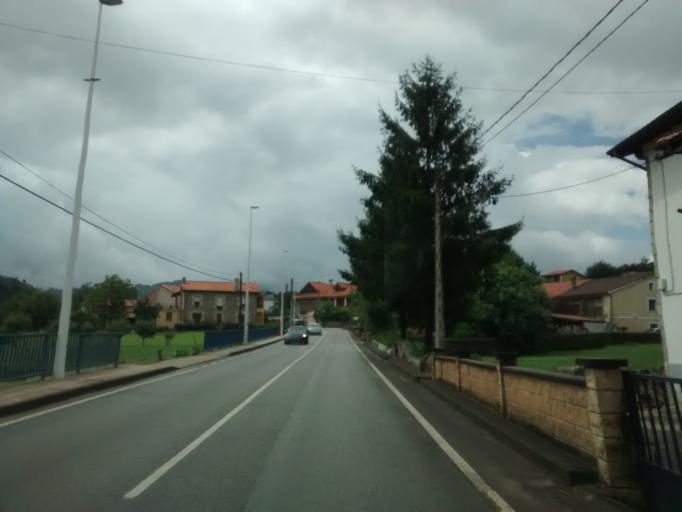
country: ES
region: Cantabria
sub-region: Provincia de Cantabria
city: Entrambasaguas
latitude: 43.3646
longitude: -3.6998
